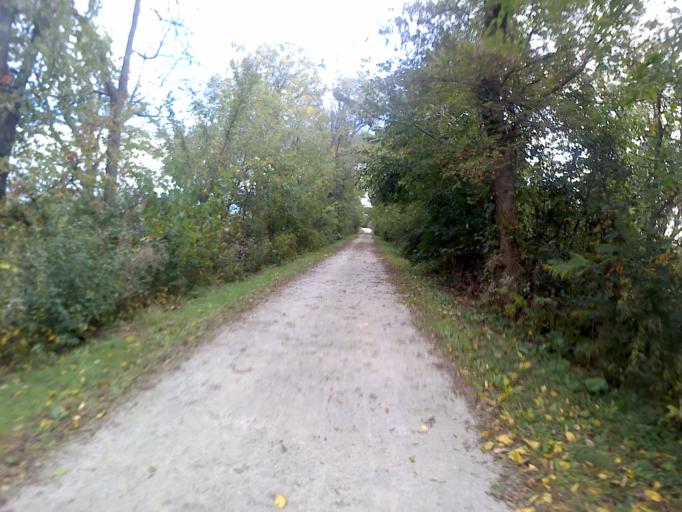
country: US
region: Illinois
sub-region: DuPage County
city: Wayne
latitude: 41.9487
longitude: -88.2389
